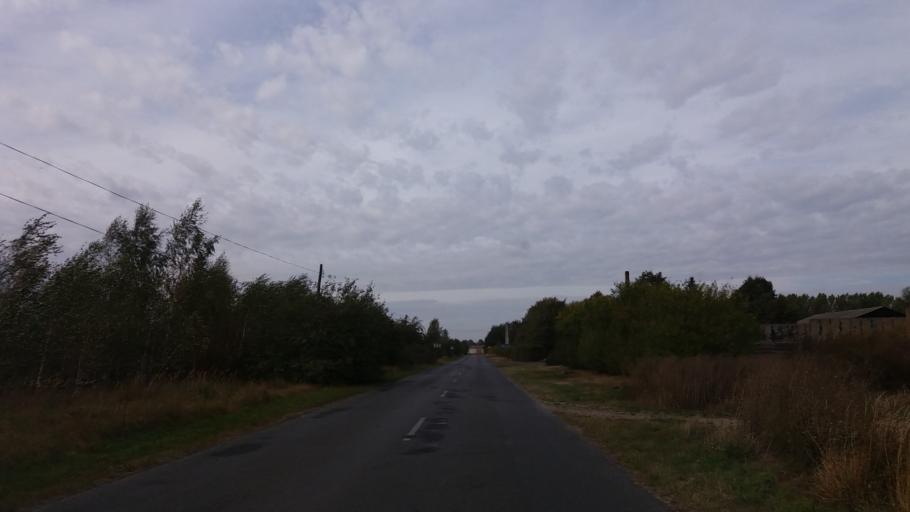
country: PL
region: Lubusz
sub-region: Powiat strzelecko-drezdenecki
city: Strzelce Krajenskie
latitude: 52.9430
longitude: 15.4594
